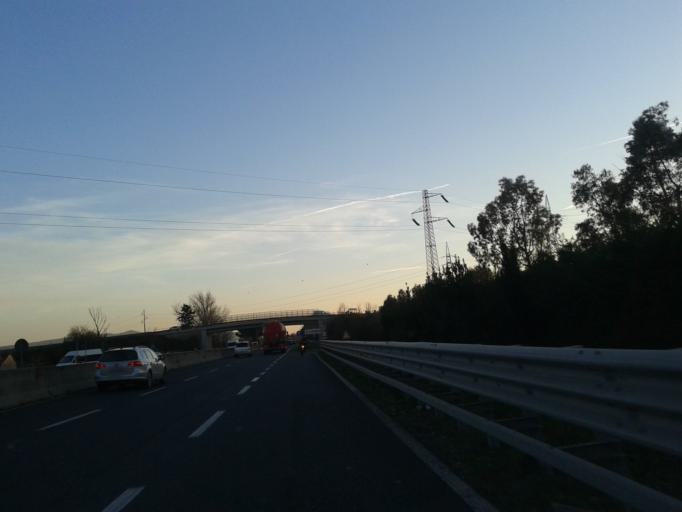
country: IT
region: Tuscany
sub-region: Provincia di Livorno
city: Livorno
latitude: 43.5633
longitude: 10.3461
